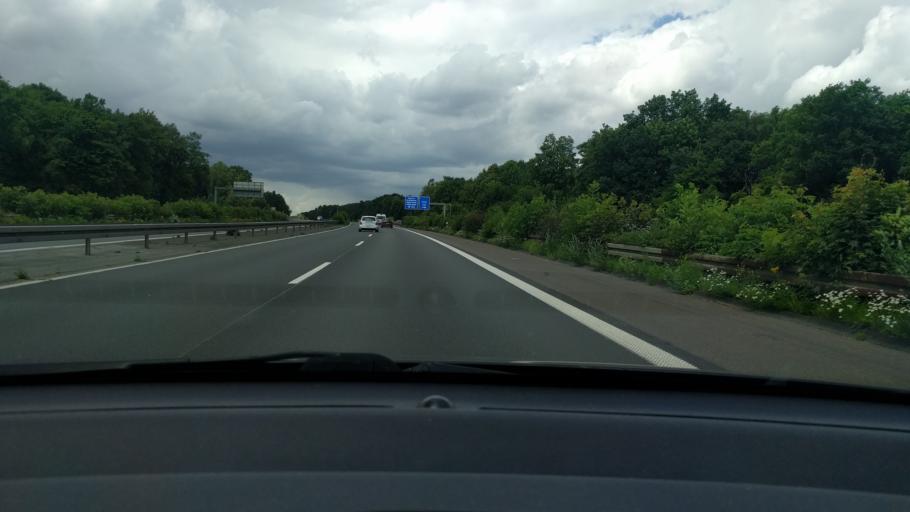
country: DE
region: North Rhine-Westphalia
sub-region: Regierungsbezirk Arnsberg
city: Bochum
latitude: 51.4953
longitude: 7.2730
